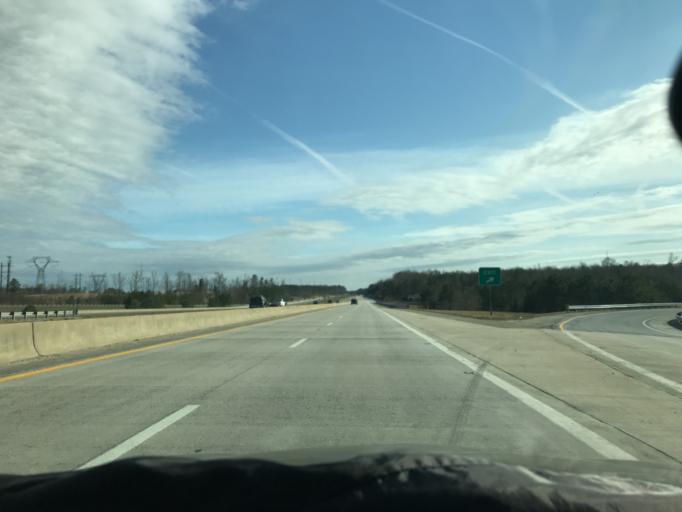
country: US
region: Virginia
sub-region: Chesterfield County
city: Brandermill
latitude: 37.4608
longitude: -77.6385
